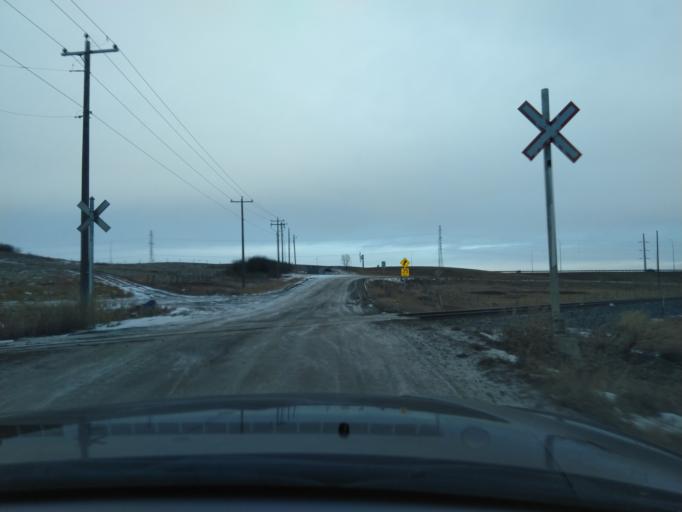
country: CA
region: Alberta
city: Airdrie
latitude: 51.1731
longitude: -114.0249
